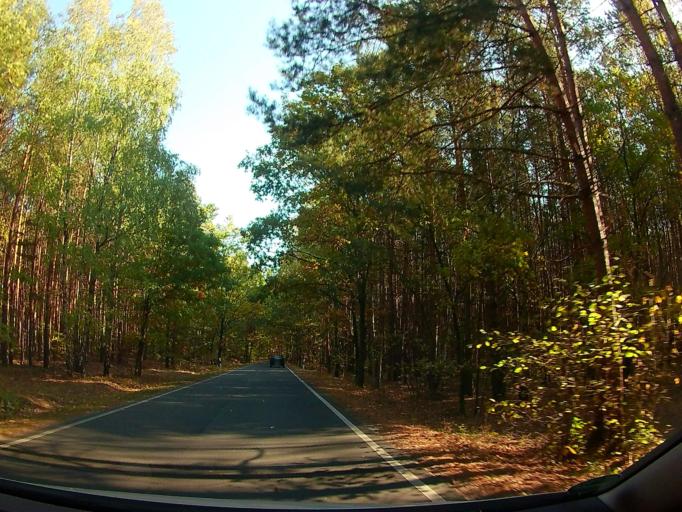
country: DE
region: Brandenburg
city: Baruth
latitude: 52.1176
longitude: 13.5082
